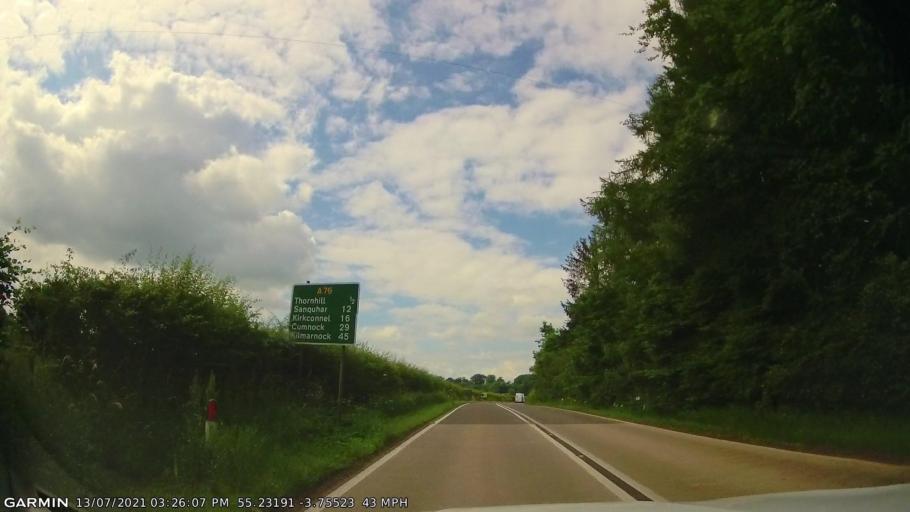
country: GB
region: Scotland
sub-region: Dumfries and Galloway
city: Thornhill
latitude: 55.2319
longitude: -3.7552
